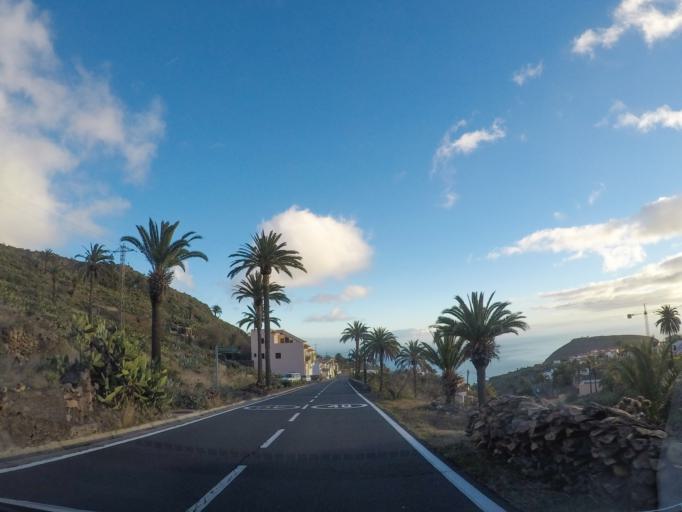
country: ES
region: Canary Islands
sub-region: Provincia de Santa Cruz de Tenerife
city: Alajero
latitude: 28.0657
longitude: -17.2378
